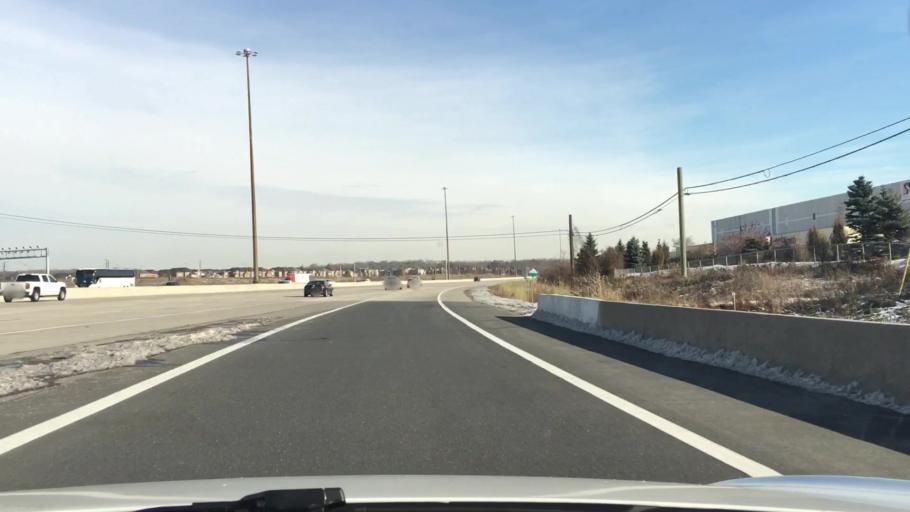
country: CA
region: Ontario
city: Concord
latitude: 43.8200
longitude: -79.4749
